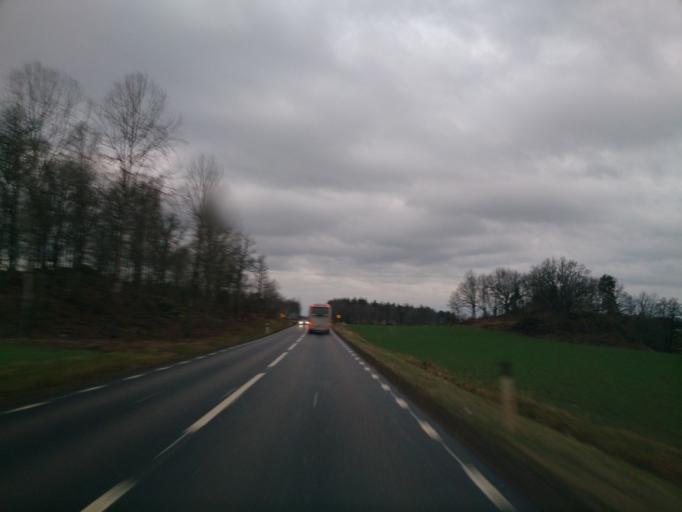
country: SE
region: OEstergoetland
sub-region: Linkopings Kommun
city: Linghem
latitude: 58.3761
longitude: 15.8065
